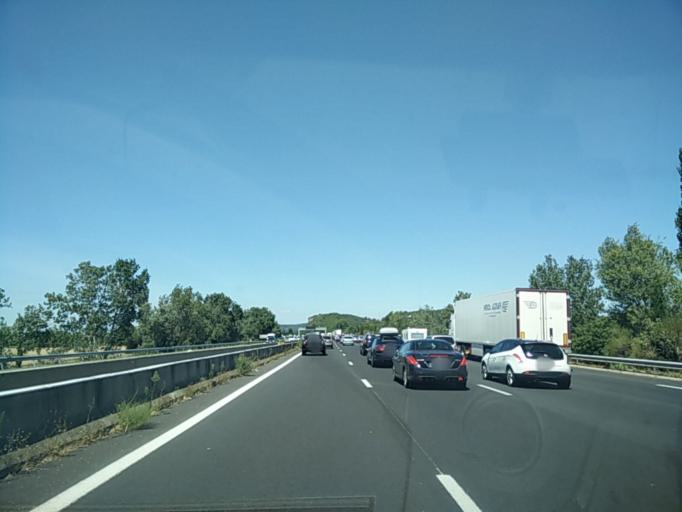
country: FR
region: Provence-Alpes-Cote d'Azur
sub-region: Departement du Vaucluse
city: Piolenc
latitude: 44.1557
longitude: 4.7712
